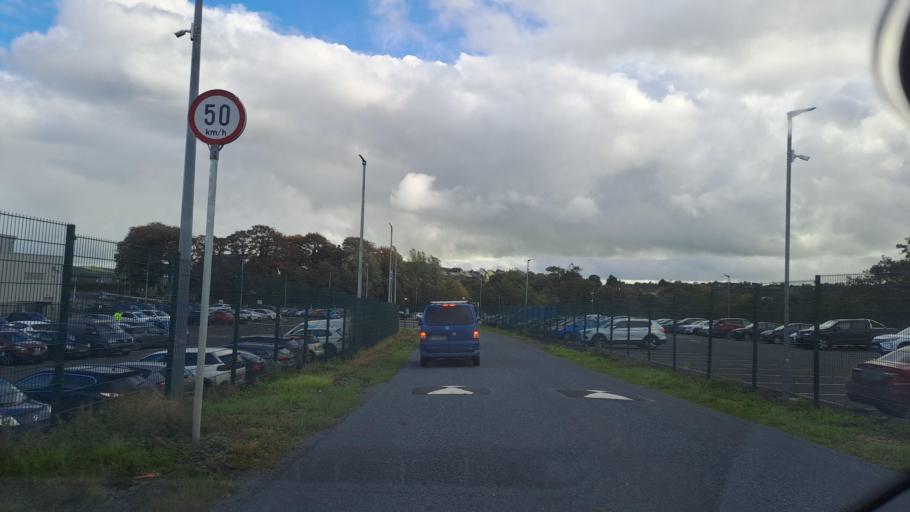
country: IE
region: Ulster
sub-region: An Cabhan
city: Bailieborough
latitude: 53.9964
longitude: -6.9047
